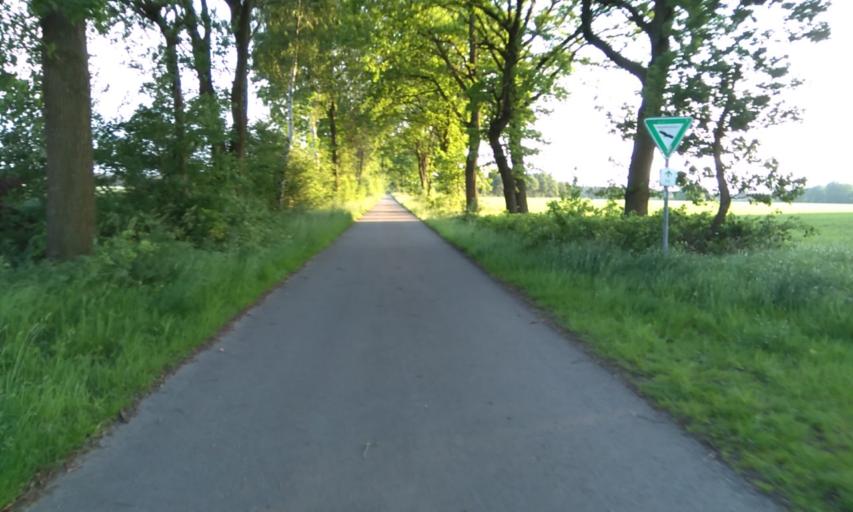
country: DE
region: Lower Saxony
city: Dollern
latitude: 53.5372
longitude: 9.5310
